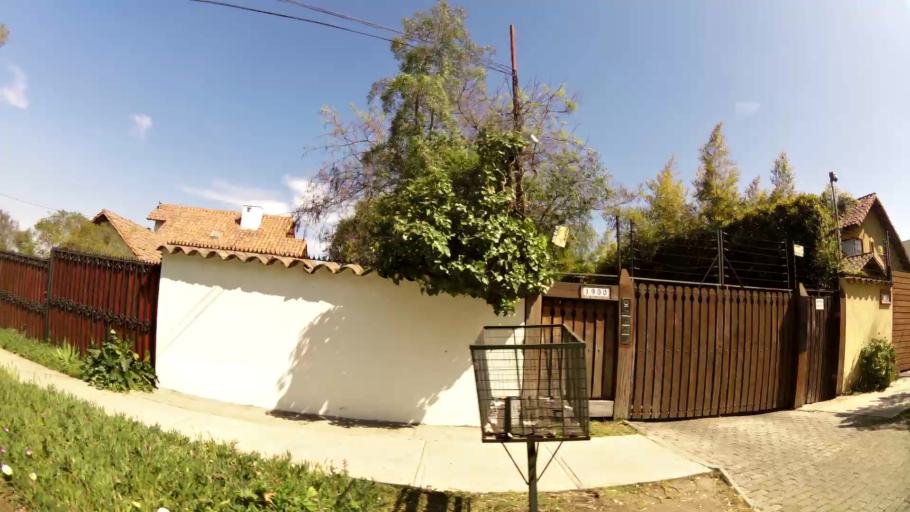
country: CL
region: Santiago Metropolitan
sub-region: Provincia de Santiago
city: Villa Presidente Frei, Nunoa, Santiago, Chile
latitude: -33.4379
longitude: -70.5299
